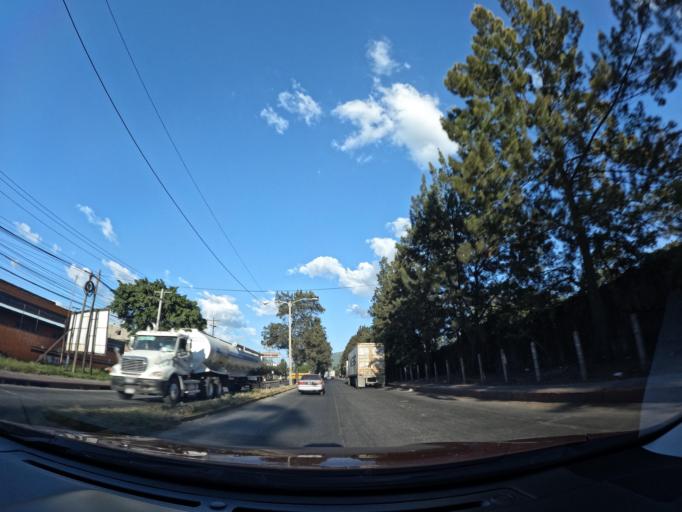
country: GT
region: Escuintla
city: Palin
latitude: 14.4071
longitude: -90.6885
